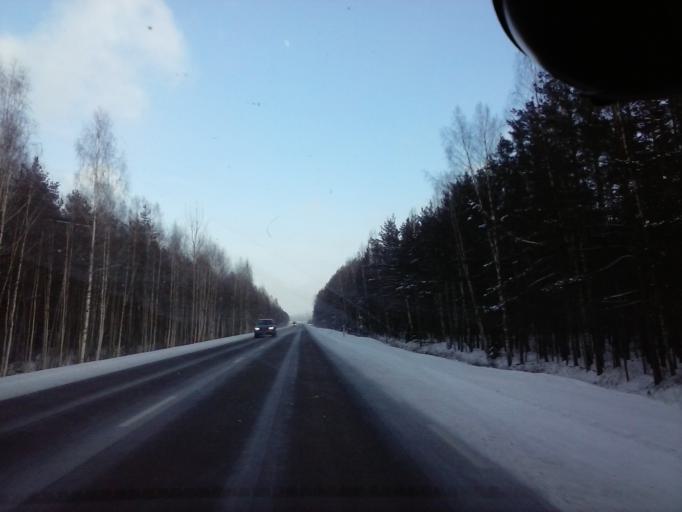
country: EE
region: Tartu
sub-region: Puhja vald
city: Puhja
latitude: 58.3269
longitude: 26.2472
